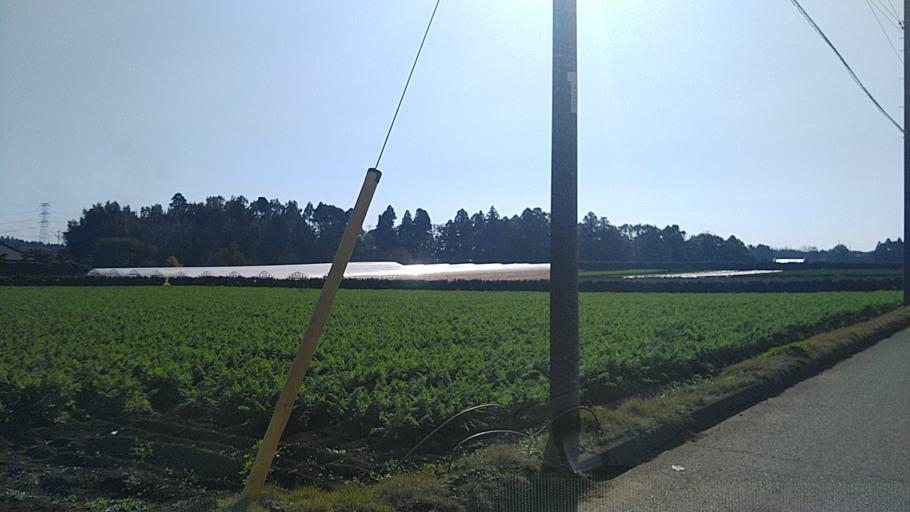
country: JP
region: Chiba
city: Sawara
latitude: 35.8482
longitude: 140.4667
